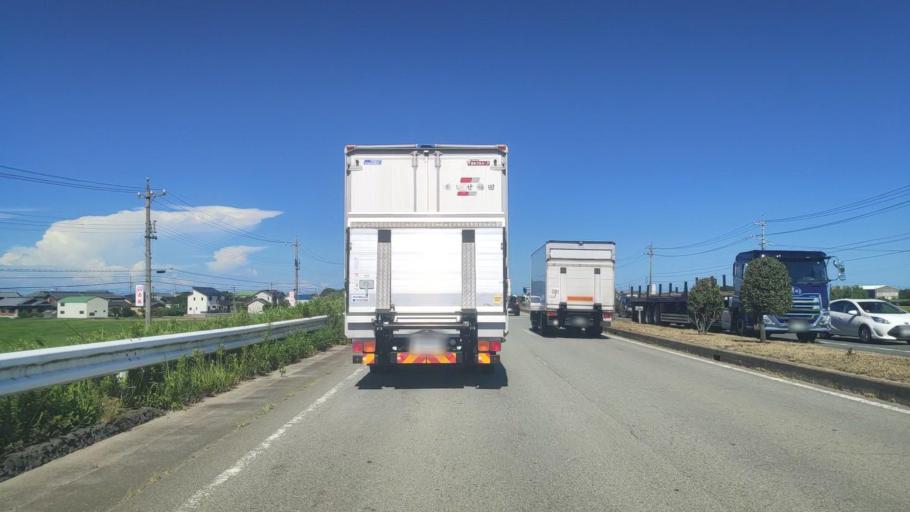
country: JP
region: Mie
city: Hisai-motomachi
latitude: 34.5870
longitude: 136.5902
